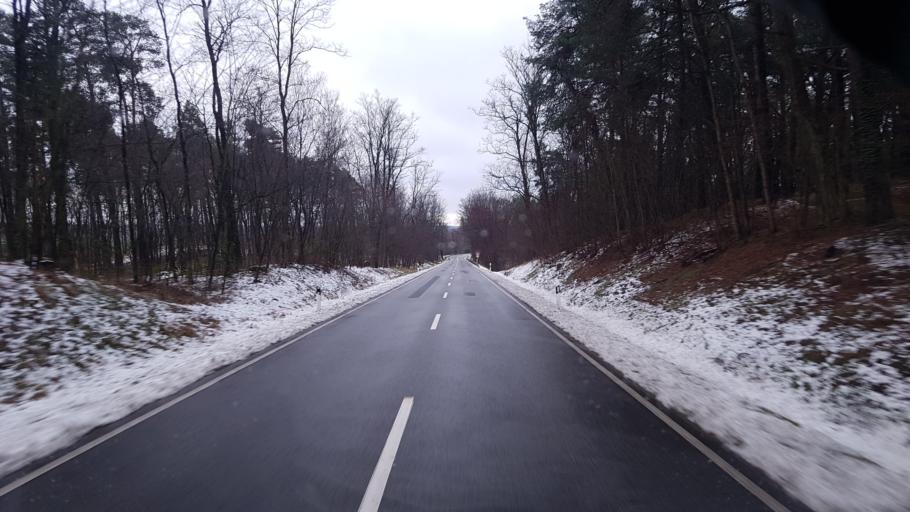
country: DE
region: Brandenburg
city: Schenkendobern
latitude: 51.9009
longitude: 14.6368
